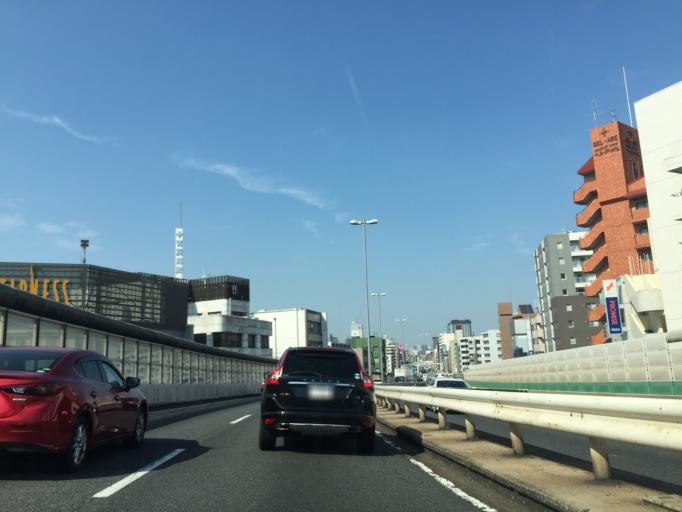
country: JP
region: Tokyo
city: Tokyo
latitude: 35.6433
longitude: 139.6708
